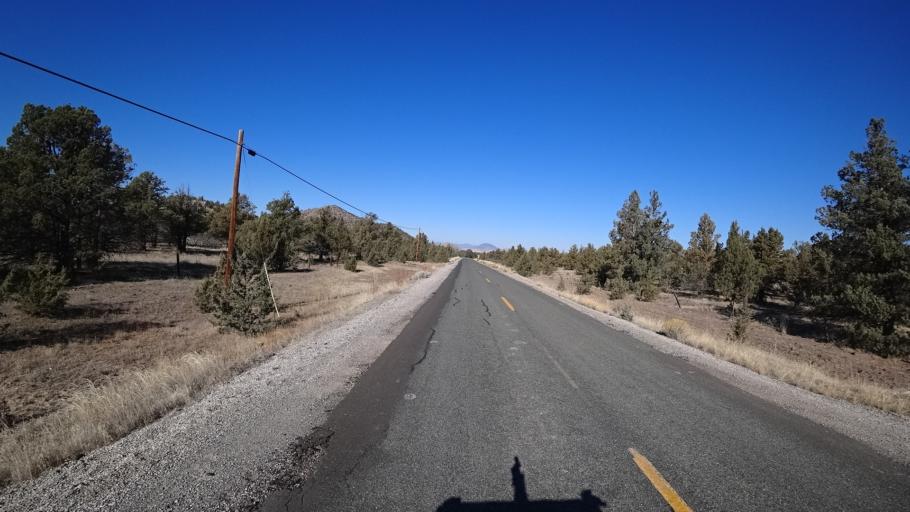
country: US
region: California
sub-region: Siskiyou County
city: Montague
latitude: 41.6593
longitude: -122.3664
